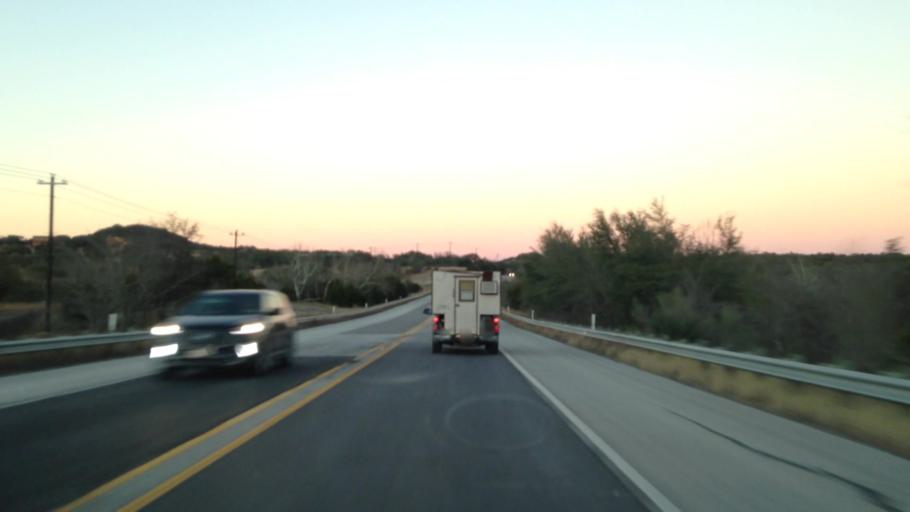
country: US
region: Texas
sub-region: Blanco County
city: Blanco
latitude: 30.1441
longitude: -98.3984
